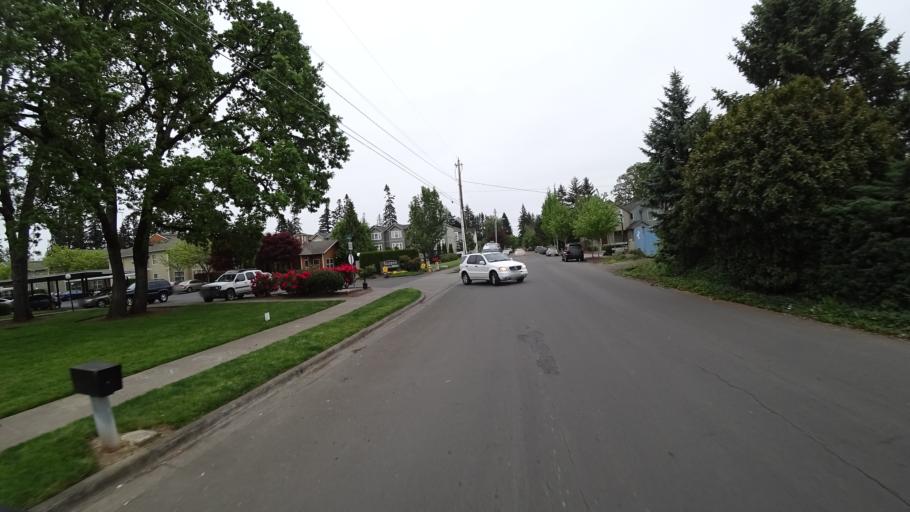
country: US
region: Oregon
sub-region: Washington County
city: Aloha
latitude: 45.5140
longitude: -122.8837
